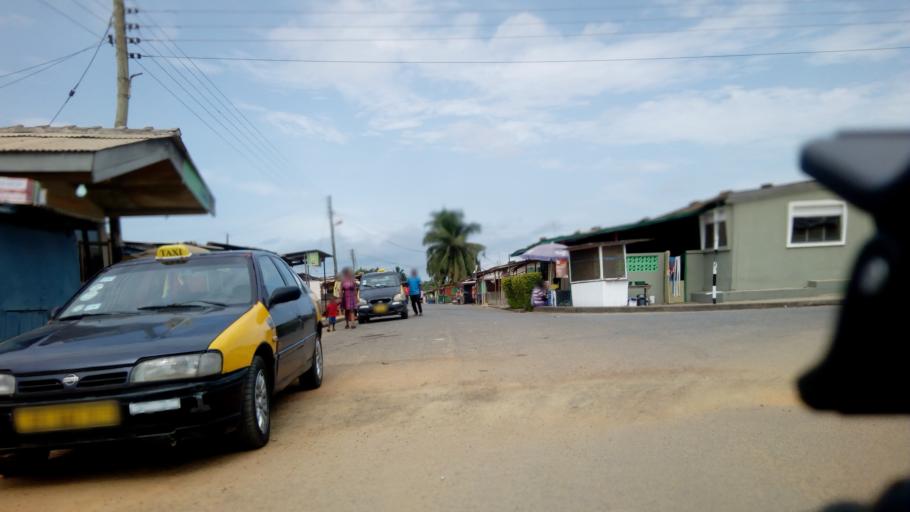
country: GH
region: Central
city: Cape Coast
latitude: 5.1024
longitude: -1.2764
